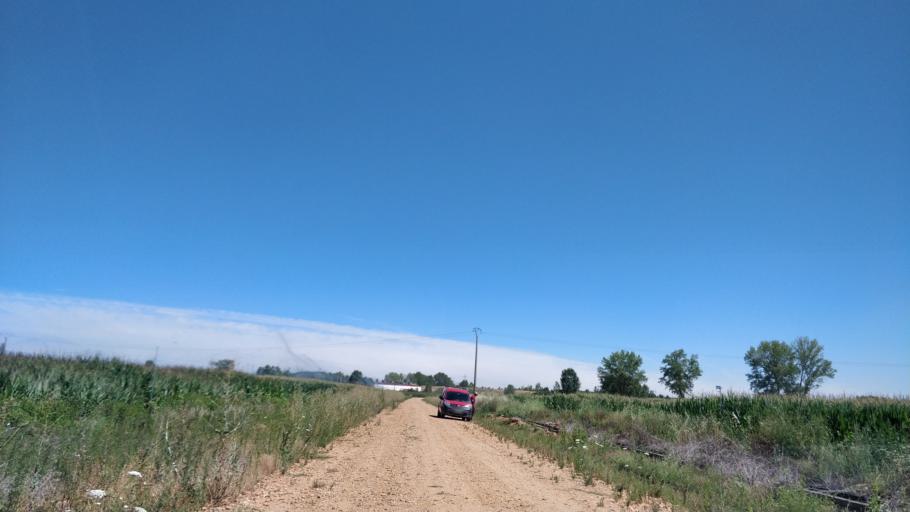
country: ES
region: Castille and Leon
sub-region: Provincia de Leon
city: Bustillo del Paramo
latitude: 42.4737
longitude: -5.8120
